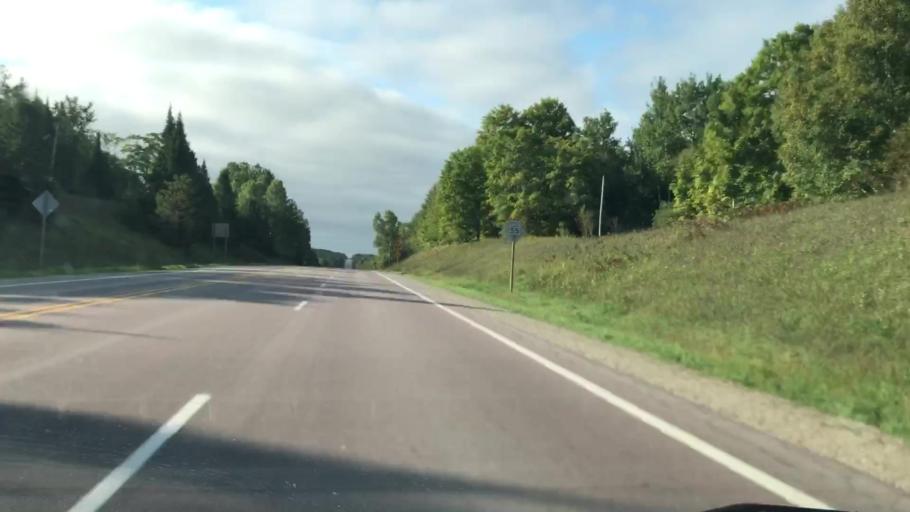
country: US
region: Michigan
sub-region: Luce County
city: Newberry
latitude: 46.3072
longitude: -85.5676
